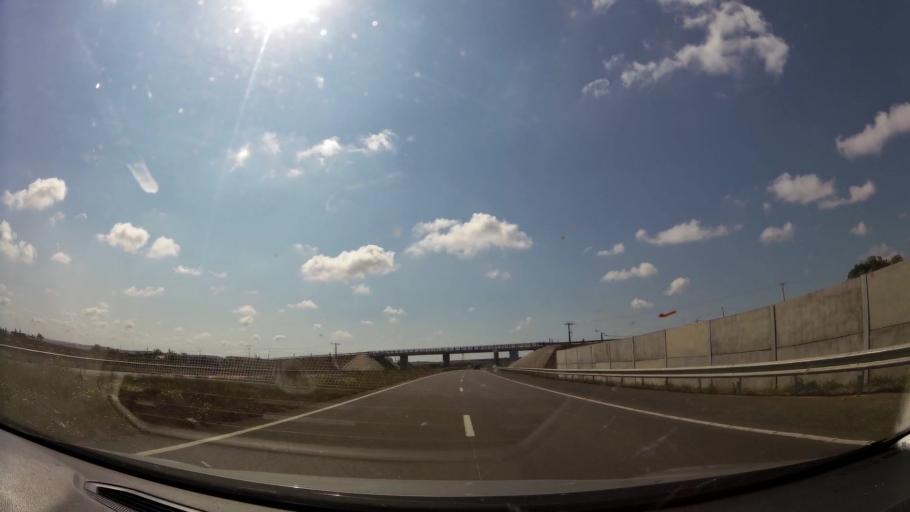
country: MA
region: Rabat-Sale-Zemmour-Zaer
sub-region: Skhirate-Temara
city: Temara
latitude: 33.8396
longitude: -6.8827
